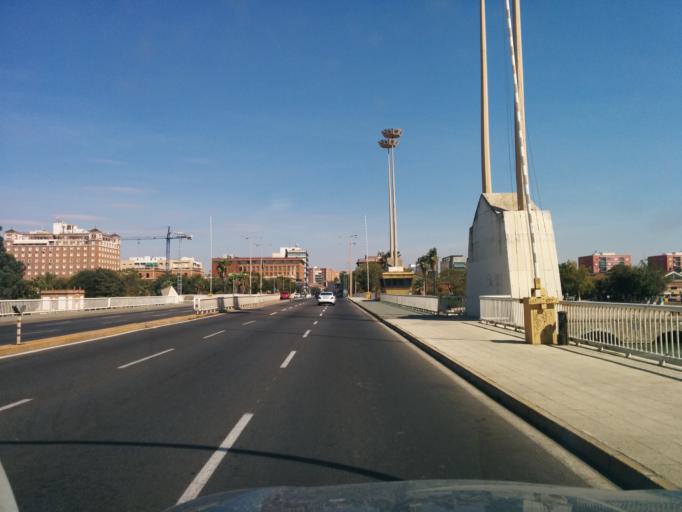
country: ES
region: Andalusia
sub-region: Provincia de Sevilla
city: Sevilla
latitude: 37.3676
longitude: -5.9931
